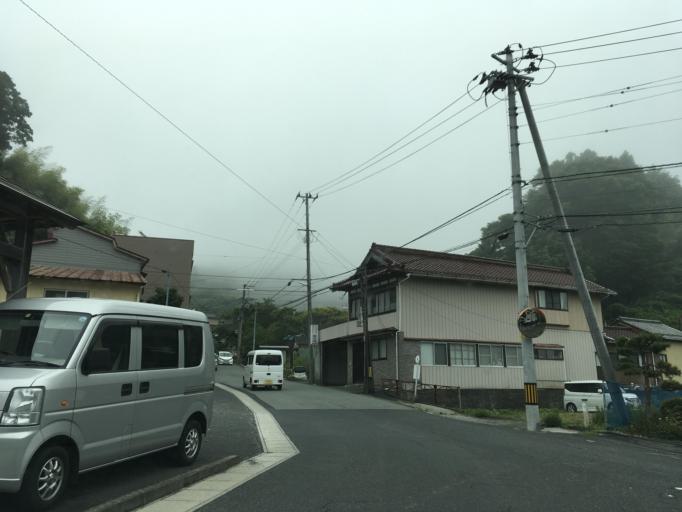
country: JP
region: Iwate
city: Ofunato
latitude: 38.9020
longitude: 141.6463
